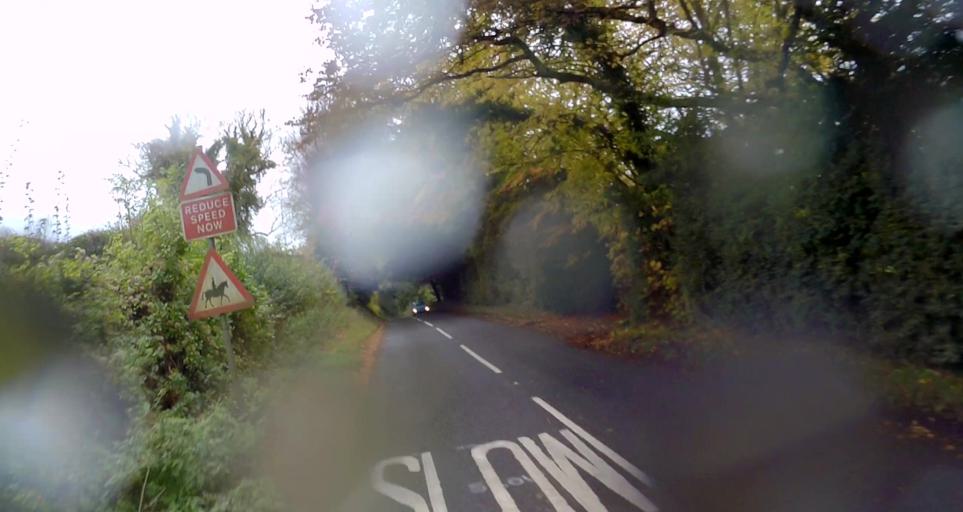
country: GB
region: England
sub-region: Hampshire
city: Kings Worthy
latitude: 51.1275
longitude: -1.1880
